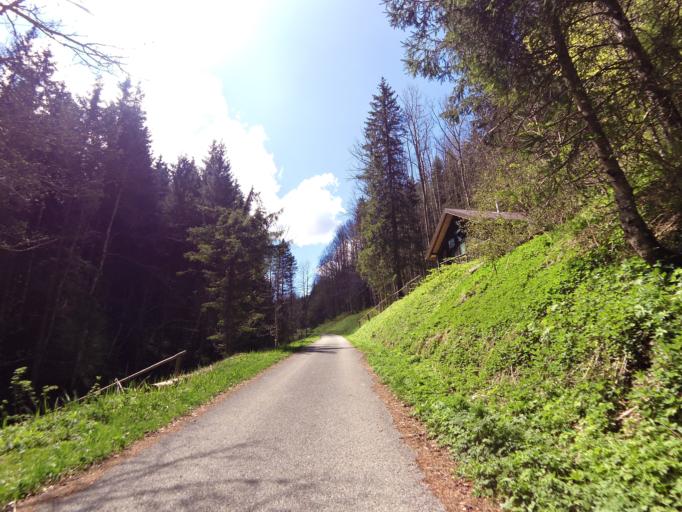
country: CH
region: Vaud
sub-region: Jura-Nord vaudois District
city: L'Abbaye
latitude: 46.6771
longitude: 6.3390
